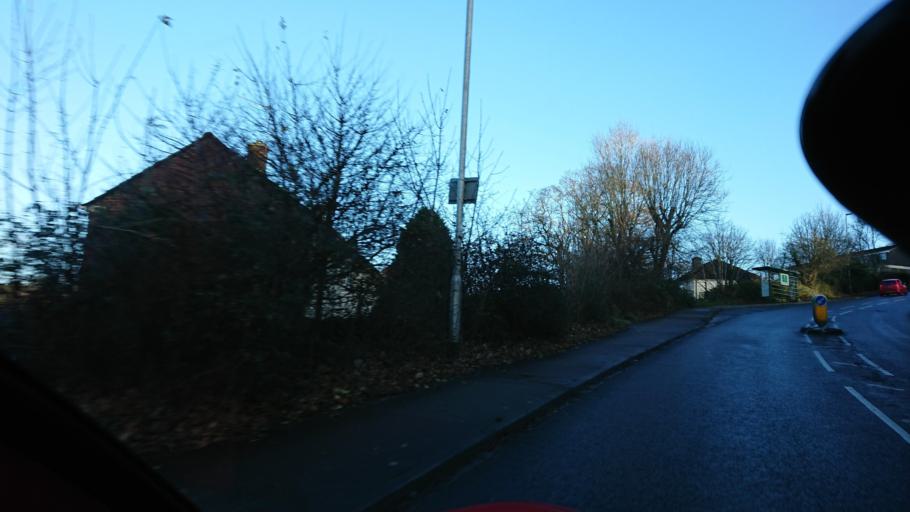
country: GB
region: England
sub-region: Plymouth
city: Plymouth
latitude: 50.4017
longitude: -4.1519
